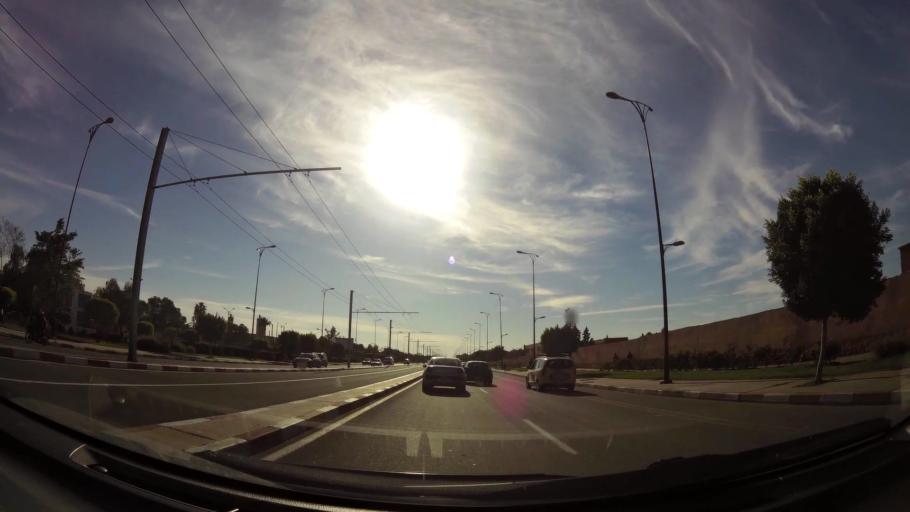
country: MA
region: Marrakech-Tensift-Al Haouz
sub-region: Marrakech
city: Marrakesh
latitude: 31.6276
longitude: -8.0480
